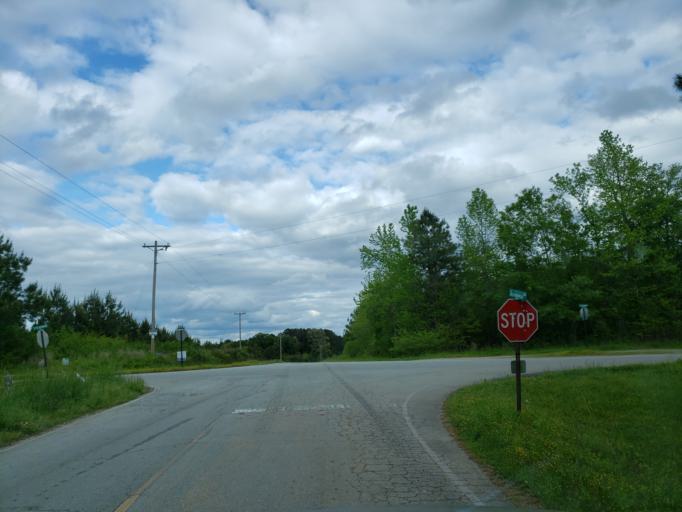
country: US
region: Georgia
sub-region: Haralson County
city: Tallapoosa
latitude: 33.7858
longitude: -85.3212
